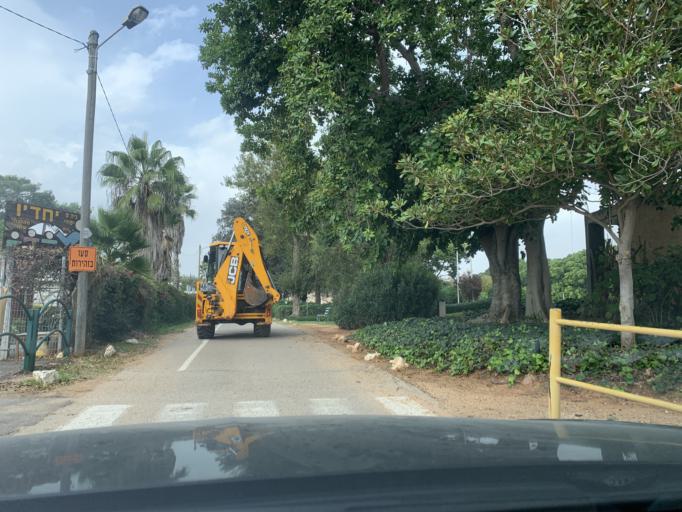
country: IL
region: Central District
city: Tirah
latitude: 32.2149
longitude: 34.9381
